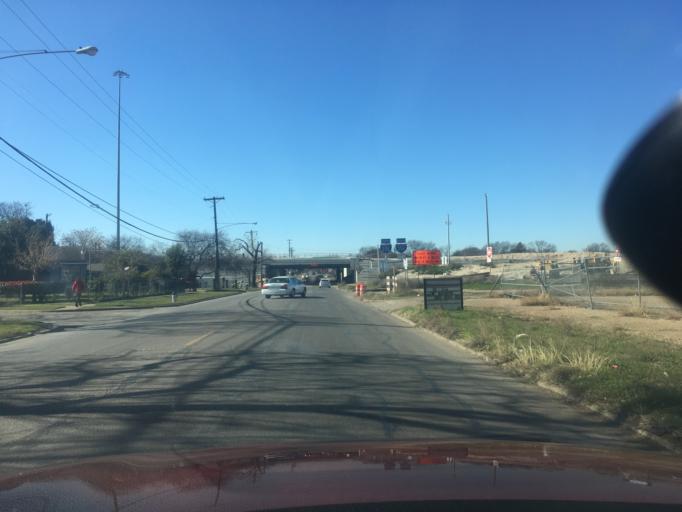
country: US
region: Texas
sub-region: Dallas County
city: Cockrell Hill
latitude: 32.7132
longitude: -96.8277
